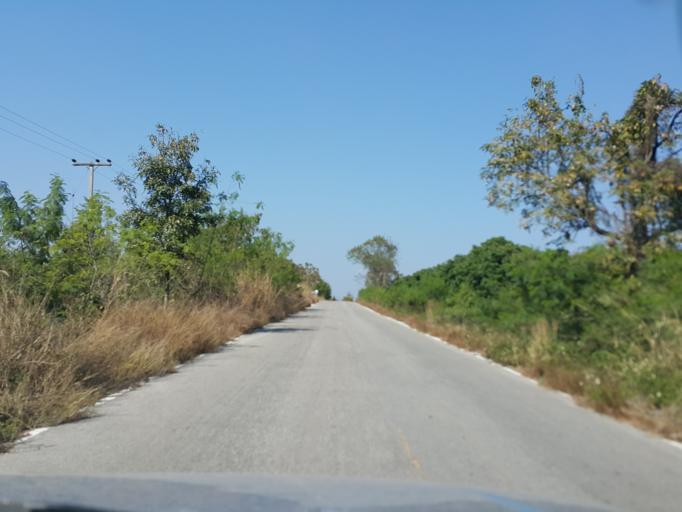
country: TH
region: Chiang Mai
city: Mae Wang
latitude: 18.5426
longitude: 98.7966
